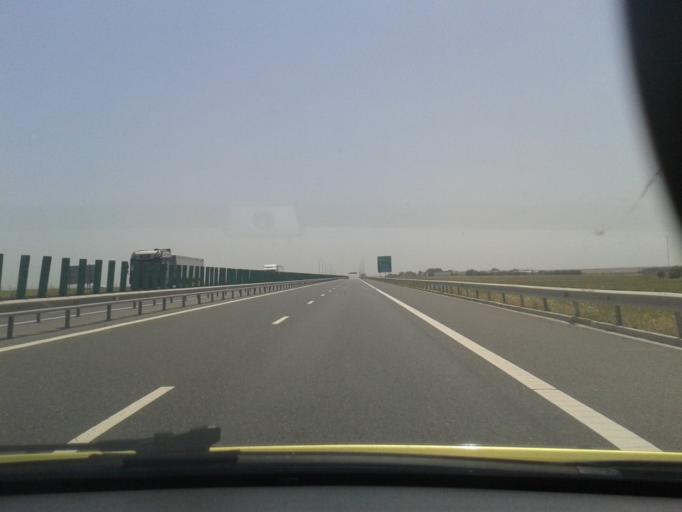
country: RO
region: Constanta
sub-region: Comuna Cumpana
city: Cumpana
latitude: 44.1821
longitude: 28.5501
